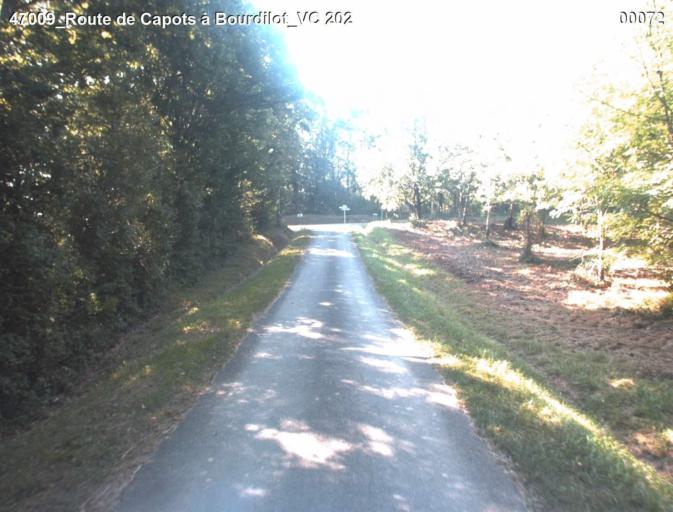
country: FR
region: Aquitaine
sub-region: Departement du Lot-et-Garonne
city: Mezin
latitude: 44.0946
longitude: 0.3028
